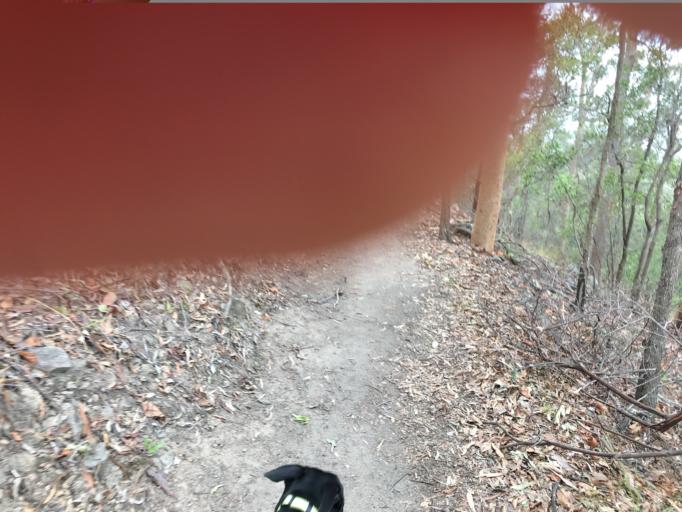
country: AU
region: Queensland
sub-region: Brisbane
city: Taringa
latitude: -27.4624
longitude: 152.9598
